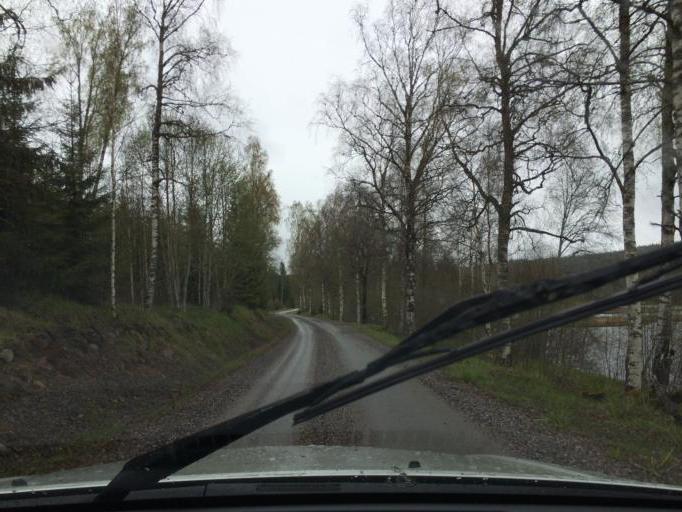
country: SE
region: Dalarna
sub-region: Ludvika Kommun
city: Abborrberget
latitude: 60.0249
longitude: 14.6363
